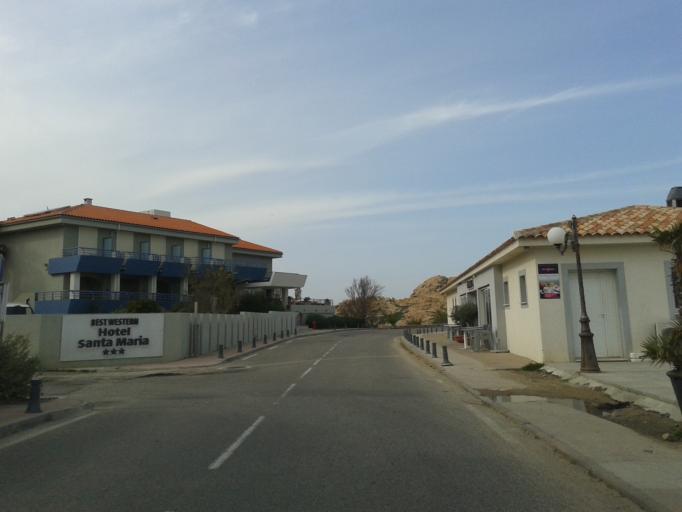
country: FR
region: Corsica
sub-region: Departement de la Haute-Corse
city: L'Ile-Rousse
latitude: 42.6381
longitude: 8.9353
